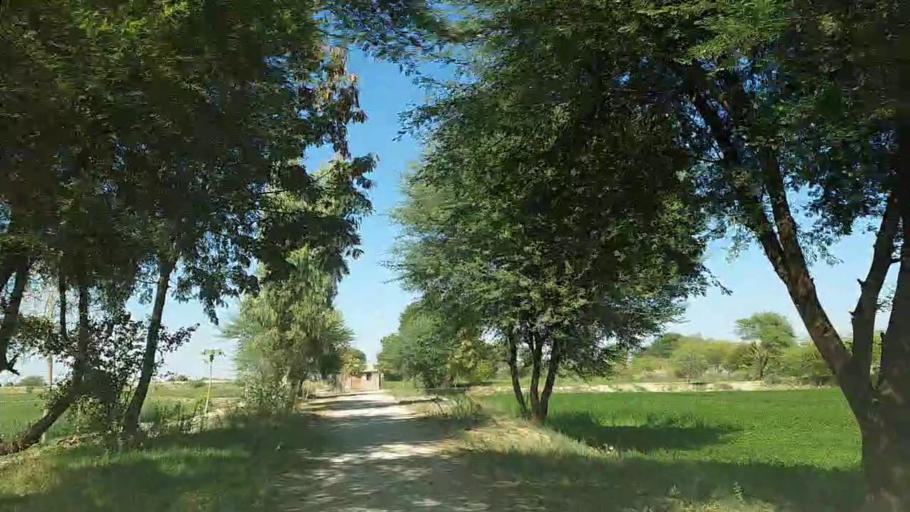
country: PK
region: Sindh
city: Samaro
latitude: 25.3051
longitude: 69.4649
